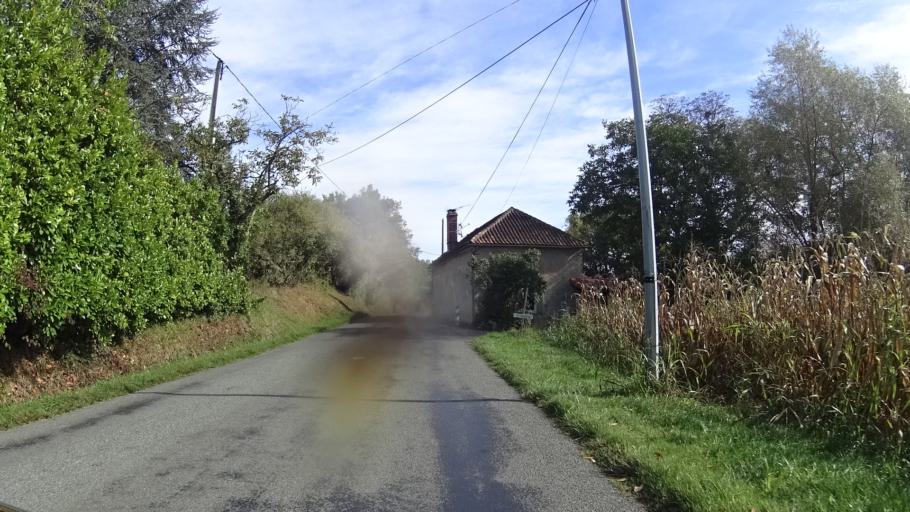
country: FR
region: Aquitaine
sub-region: Departement du Lot-et-Garonne
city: Castelculier
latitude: 44.2007
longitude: 0.7255
